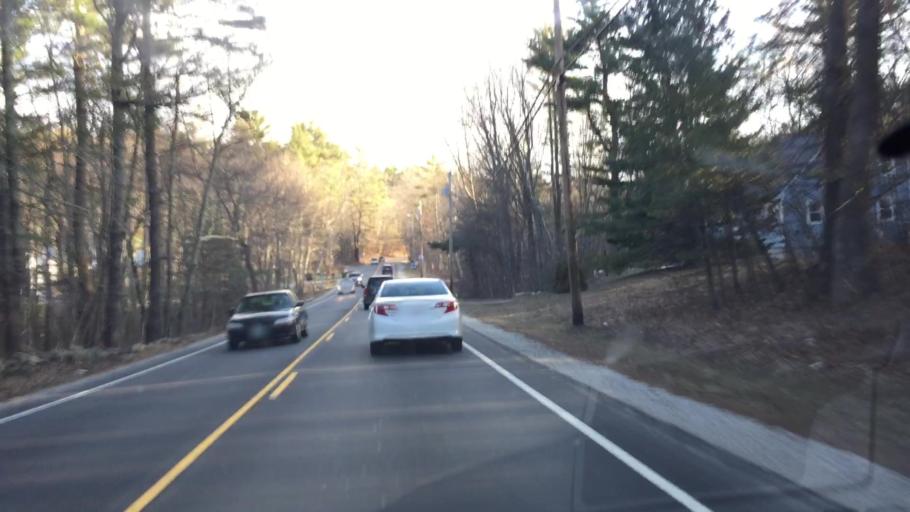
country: US
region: New Hampshire
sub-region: Rockingham County
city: Londonderry
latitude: 42.8286
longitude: -71.3653
